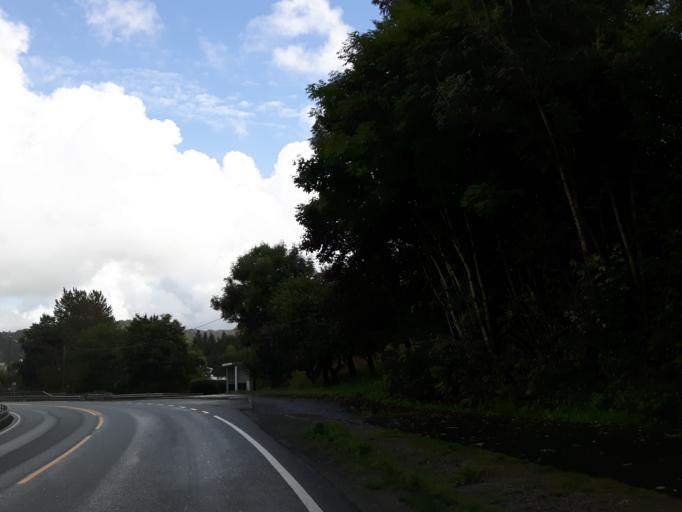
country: NO
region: Vest-Agder
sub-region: Lyngdal
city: Lyngdal
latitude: 58.1491
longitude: 7.0887
